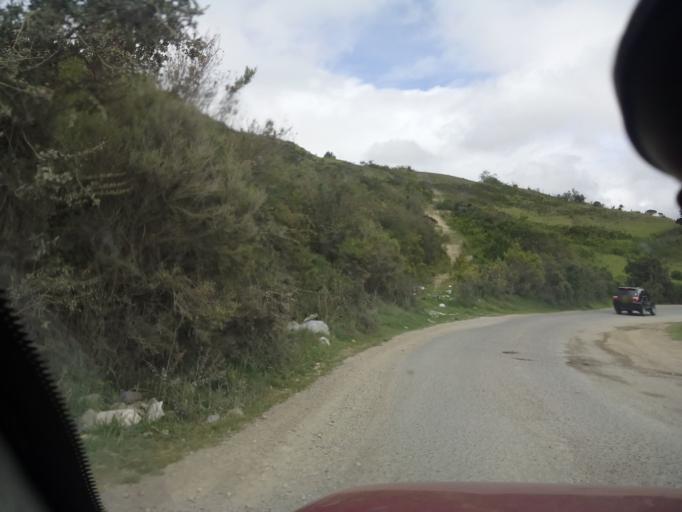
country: CO
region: Boyaca
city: Combita
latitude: 5.6351
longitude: -73.3443
